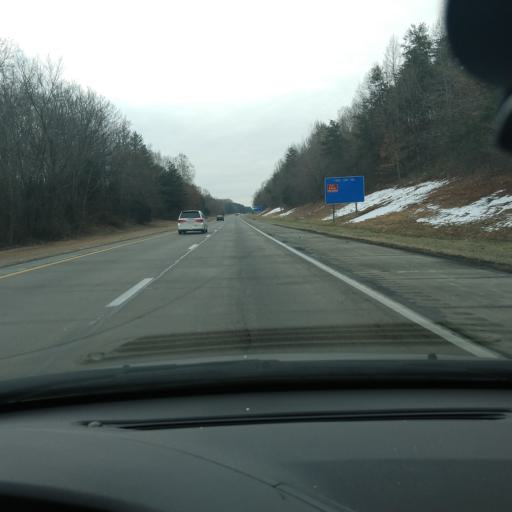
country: US
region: North Carolina
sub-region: Davidson County
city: Midway
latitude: 35.9811
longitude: -80.2339
